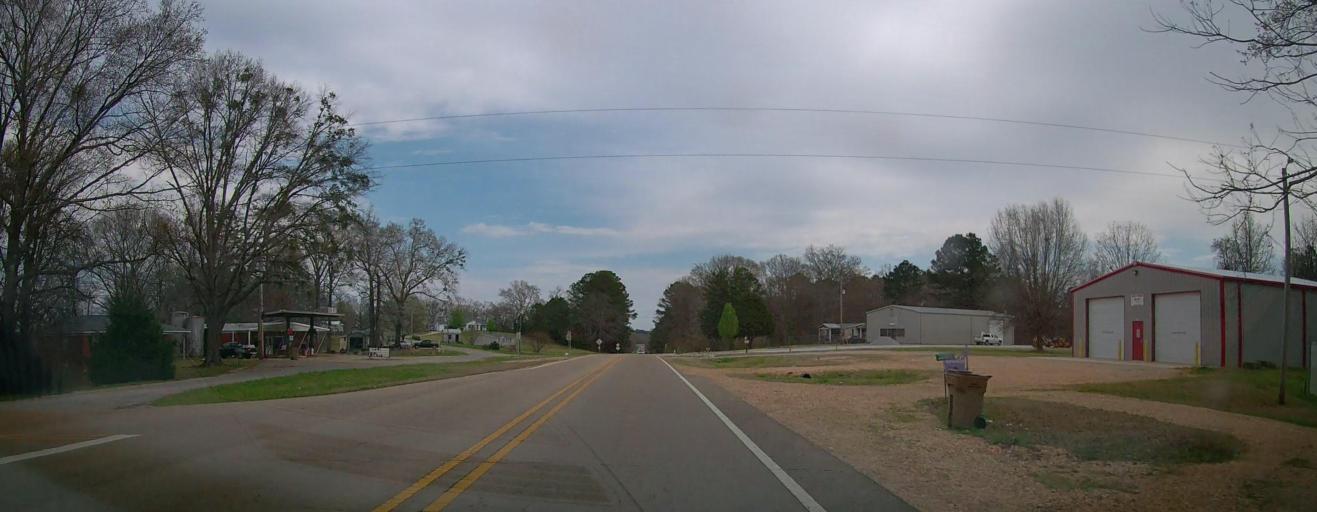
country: US
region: Mississippi
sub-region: Itawamba County
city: Mantachie
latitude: 34.2550
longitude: -88.4901
